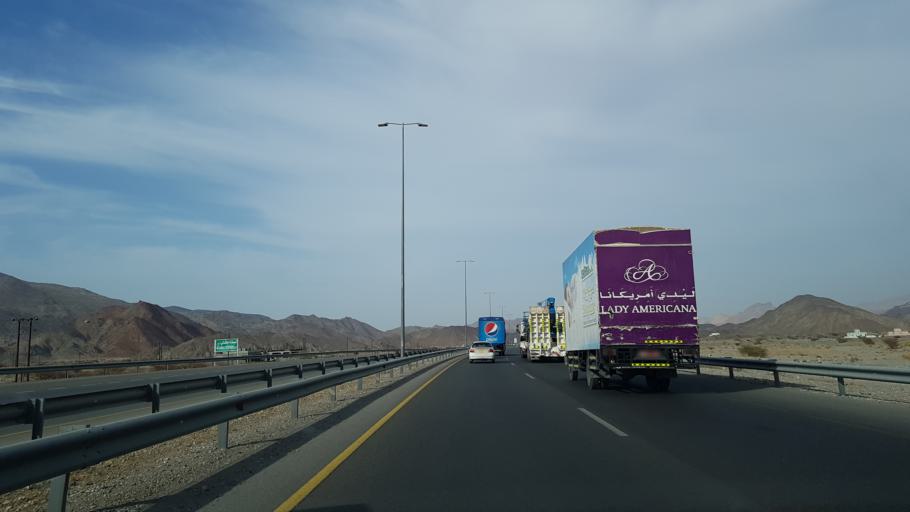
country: OM
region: Muhafazat ad Dakhiliyah
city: Sufalat Sama'il
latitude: 23.3796
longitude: 58.0528
